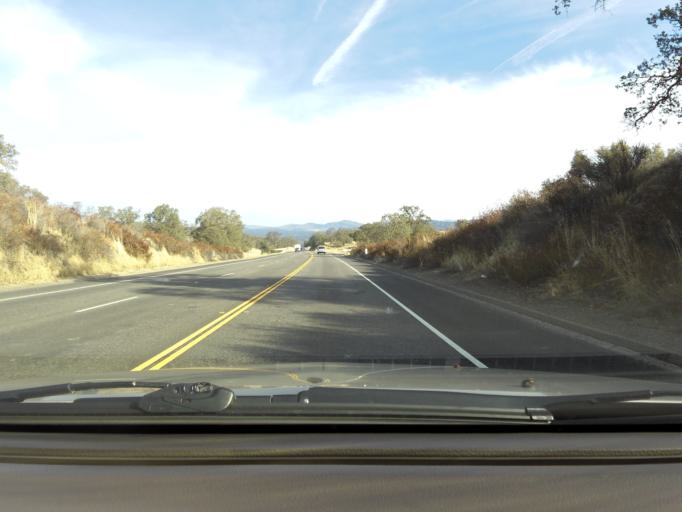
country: US
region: California
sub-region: Madera County
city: Yosemite Lakes
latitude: 37.1335
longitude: -119.7343
